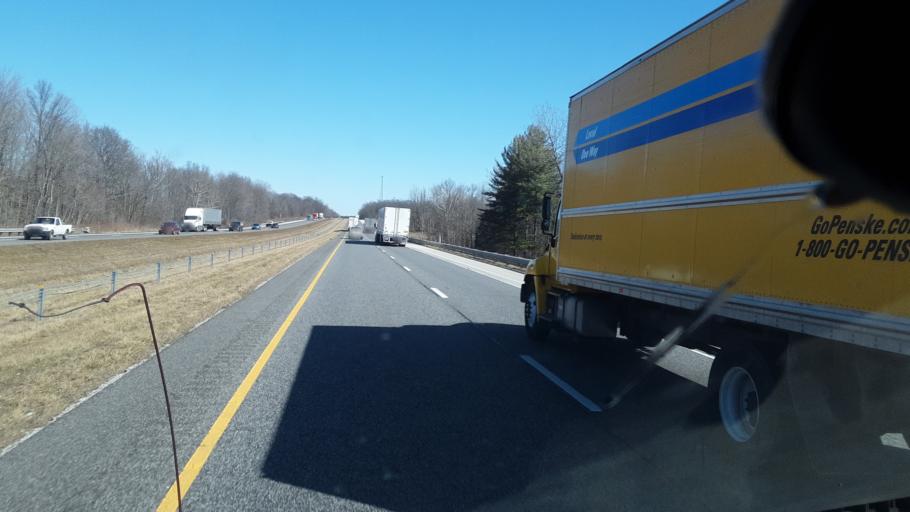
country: US
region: Indiana
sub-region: Clay County
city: Brazil
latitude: 39.4641
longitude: -87.0660
